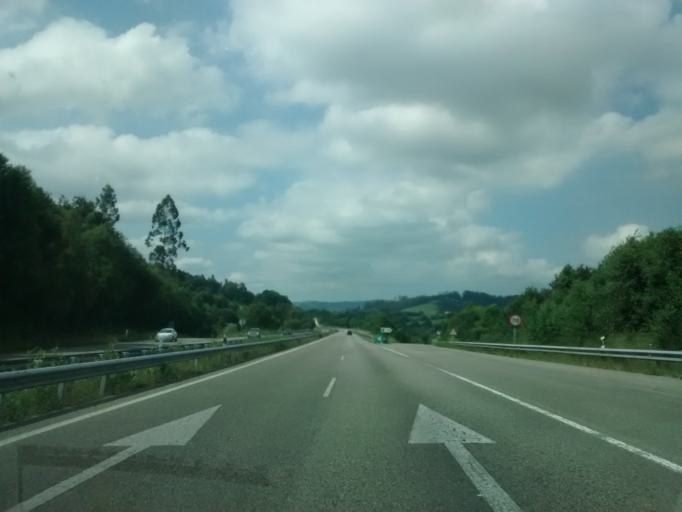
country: ES
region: Asturias
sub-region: Province of Asturias
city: Pola de Siero
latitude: 43.3522
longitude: -5.6808
